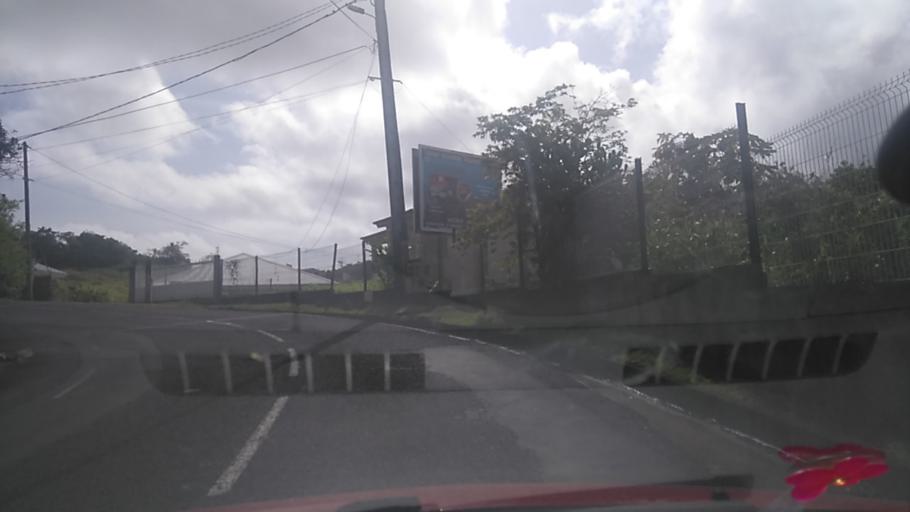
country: MQ
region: Martinique
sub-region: Martinique
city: Saint-Esprit
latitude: 14.5685
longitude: -60.9347
